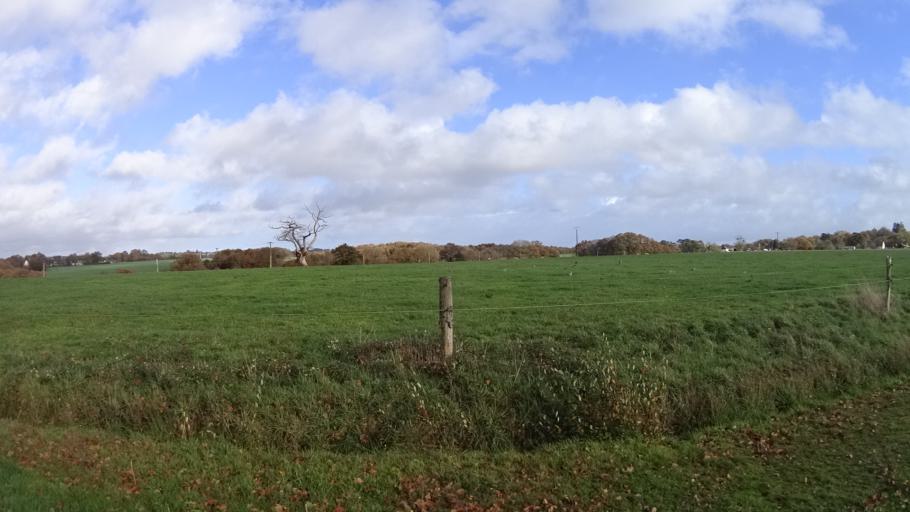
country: FR
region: Pays de la Loire
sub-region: Departement de la Loire-Atlantique
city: Saint-Nicolas-de-Redon
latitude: 47.6234
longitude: -2.0699
